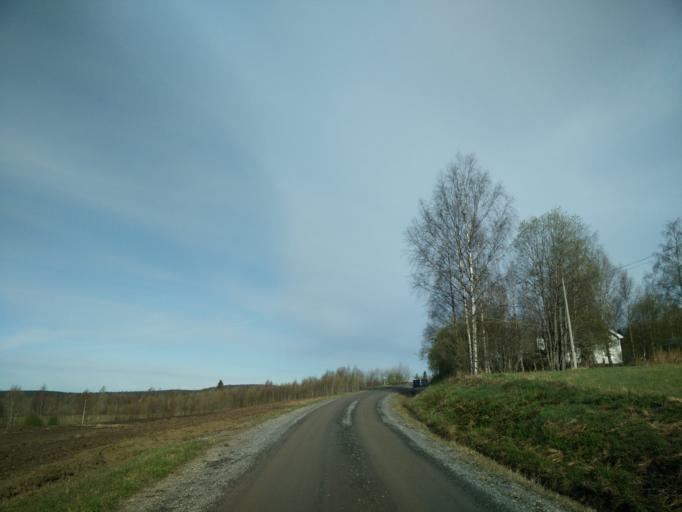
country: SE
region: Vaesternorrland
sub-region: Timra Kommun
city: Soraker
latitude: 62.6143
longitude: 17.7018
